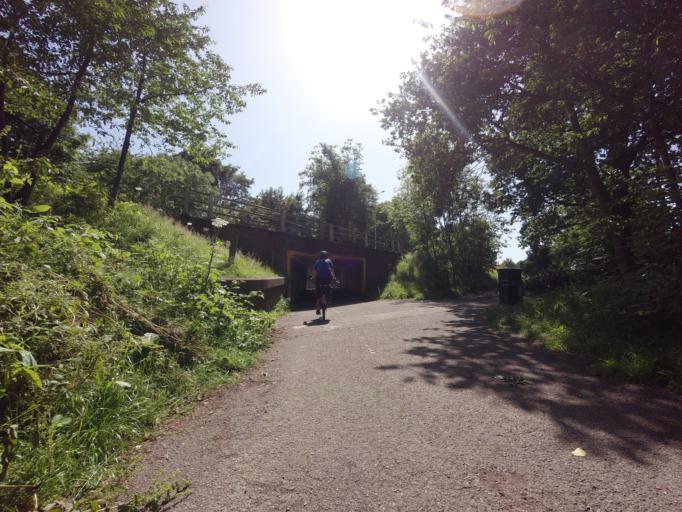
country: GB
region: Scotland
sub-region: Highland
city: Inverness
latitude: 57.4862
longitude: -4.1408
